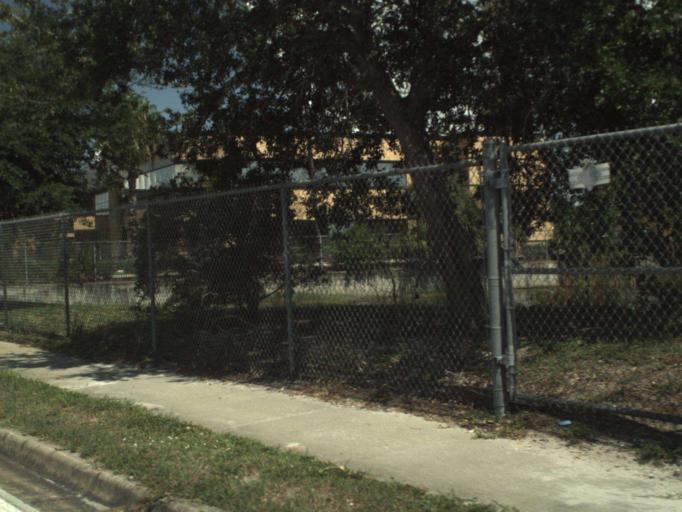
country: US
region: Florida
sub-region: Brevard County
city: West Melbourne
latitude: 28.1289
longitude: -80.6565
